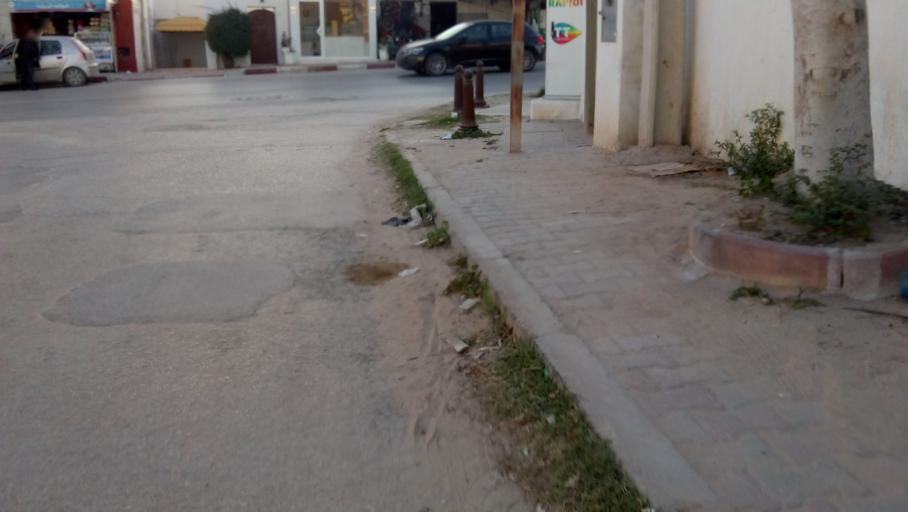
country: TN
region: Safaqis
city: Sfax
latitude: 34.7494
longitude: 10.7347
